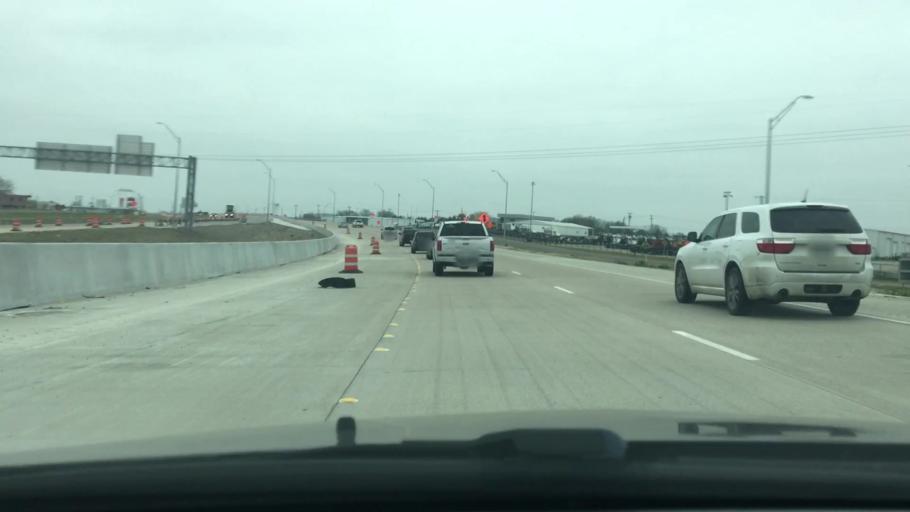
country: US
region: Texas
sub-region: Navarro County
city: Corsicana
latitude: 32.0634
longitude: -96.4520
